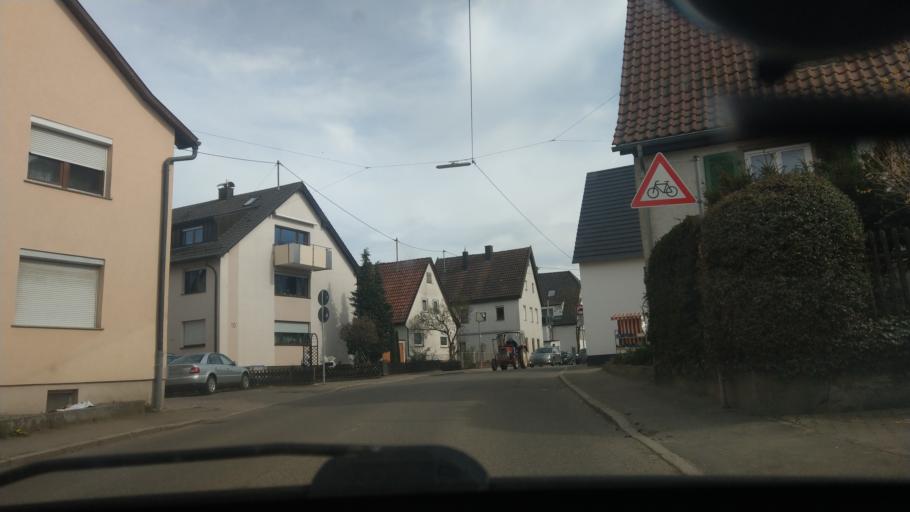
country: DE
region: Baden-Wuerttemberg
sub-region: Regierungsbezirk Stuttgart
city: Filderstadt
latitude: 48.6758
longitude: 9.2364
